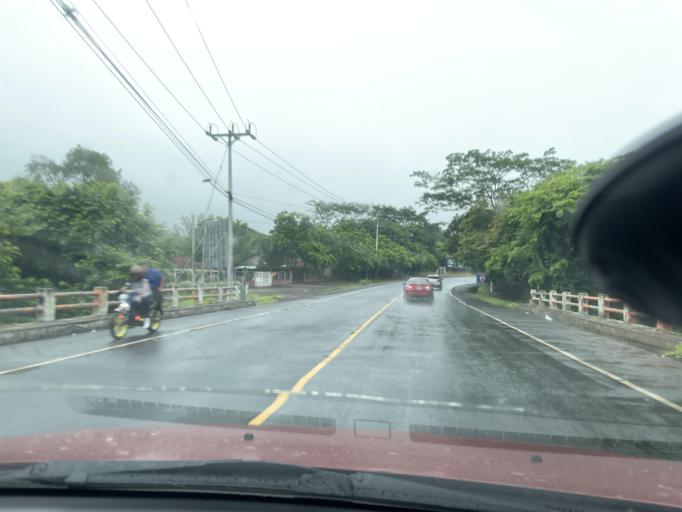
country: SV
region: San Miguel
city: San Miguel
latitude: 13.5583
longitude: -88.1105
